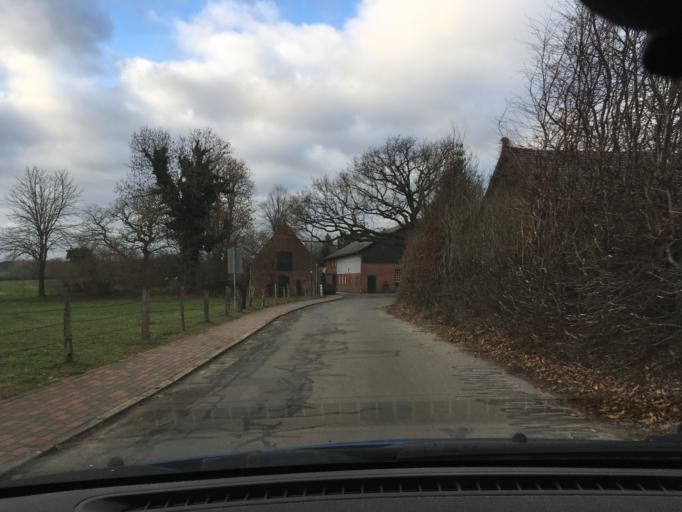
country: DE
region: Schleswig-Holstein
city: Kaaks
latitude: 53.9864
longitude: 9.4786
